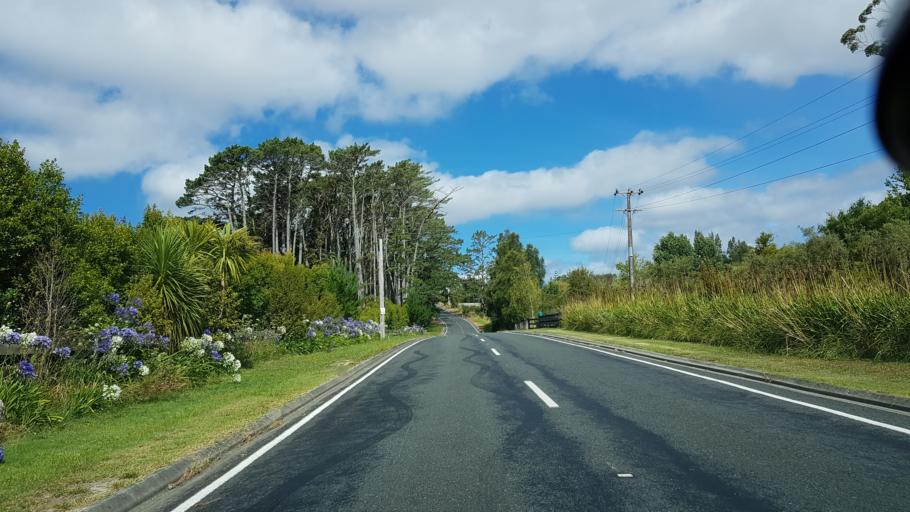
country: NZ
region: Auckland
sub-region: Auckland
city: Rothesay Bay
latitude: -36.6904
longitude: 174.6747
